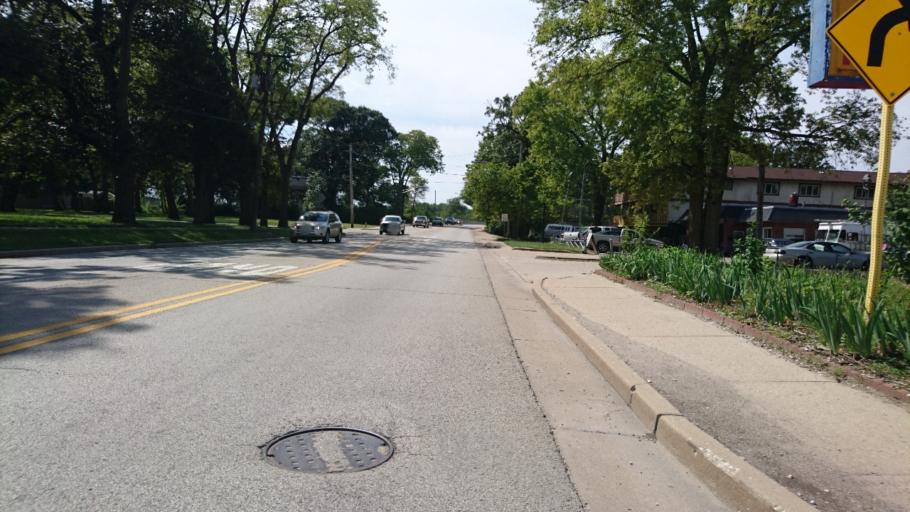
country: US
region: Illinois
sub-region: Will County
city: Wilmington
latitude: 41.3068
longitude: -88.1491
